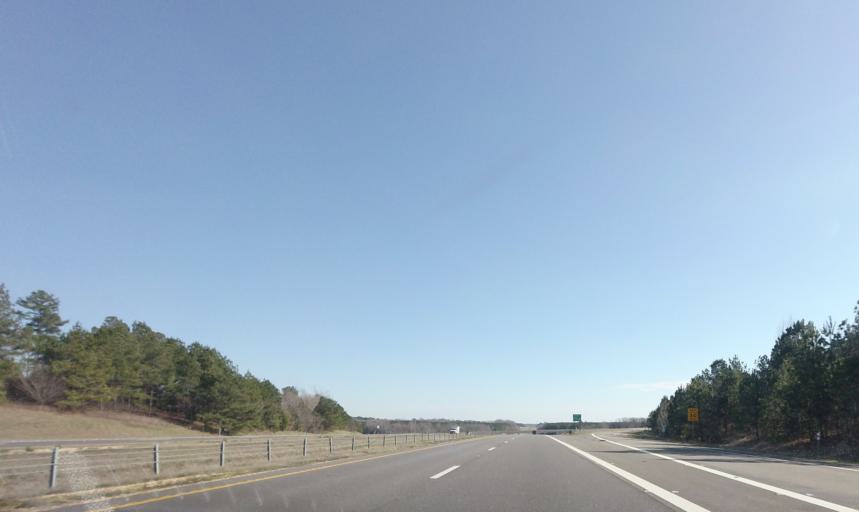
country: US
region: Mississippi
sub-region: Union County
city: New Albany
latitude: 34.5518
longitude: -89.1307
